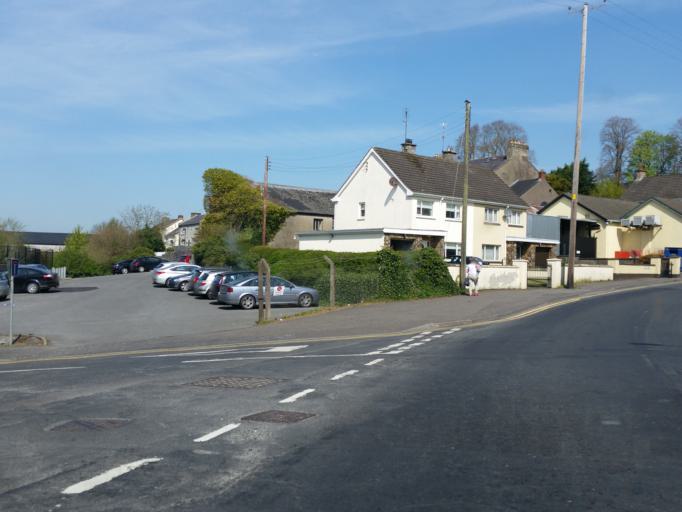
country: GB
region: Northern Ireland
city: Lisnaskea
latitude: 54.2536
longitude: -7.4458
